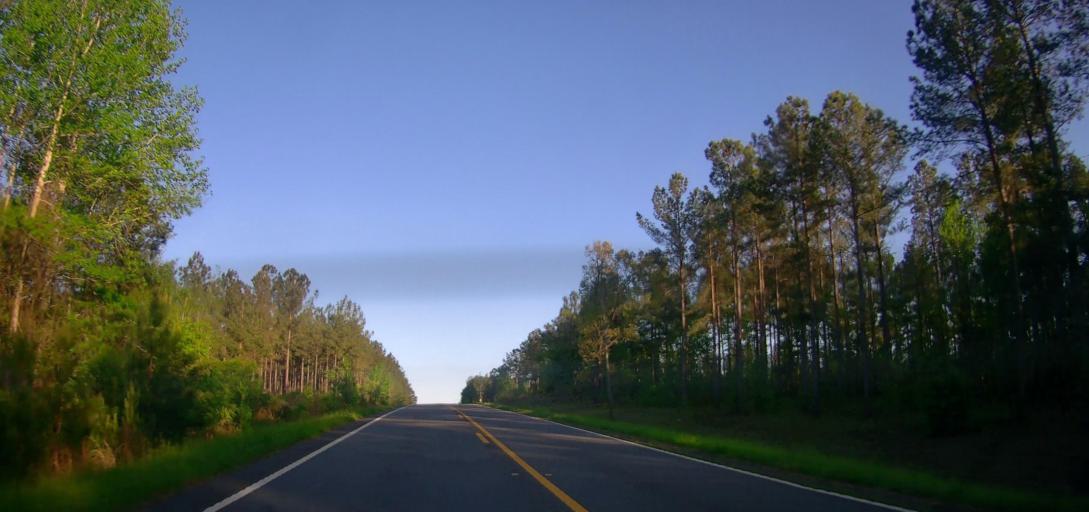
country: US
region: Georgia
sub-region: Schley County
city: Ellaville
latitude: 32.3522
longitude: -84.3810
